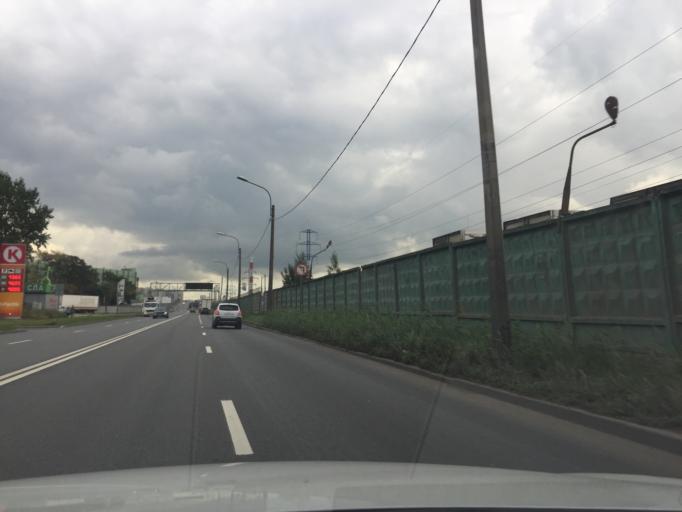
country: RU
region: St.-Petersburg
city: Dachnoye
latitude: 59.8377
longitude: 30.3035
